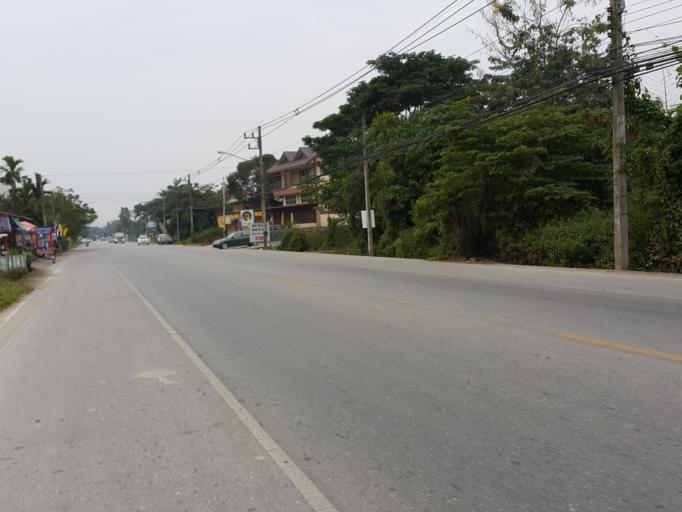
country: TH
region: Chiang Mai
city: San Kamphaeng
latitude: 18.7882
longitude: 99.0988
